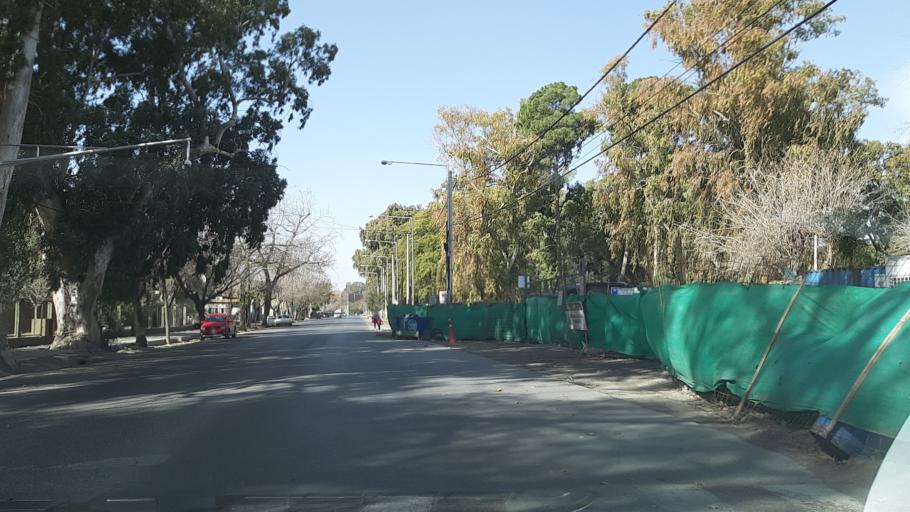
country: AR
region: San Juan
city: San Juan
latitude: -31.5304
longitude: -68.5424
